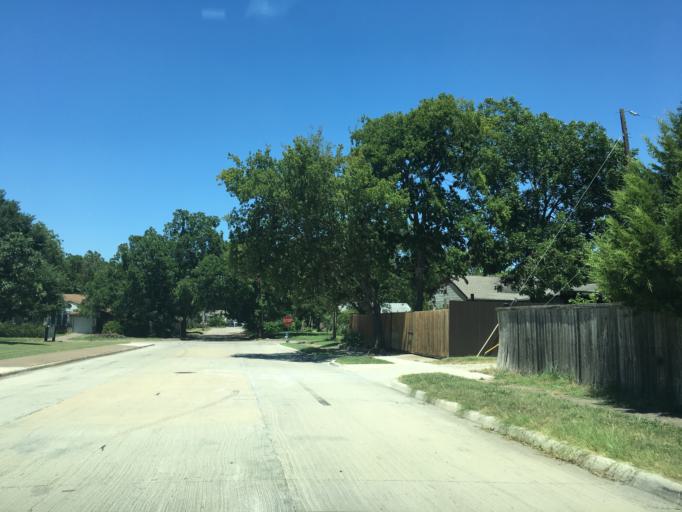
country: US
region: Texas
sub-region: Dallas County
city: Garland
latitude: 32.8477
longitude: -96.6745
